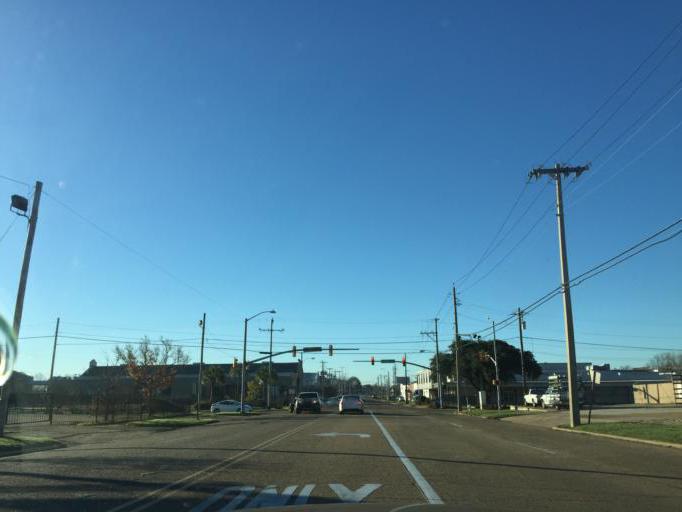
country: US
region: Mississippi
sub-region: Hinds County
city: Jackson
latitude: 32.2910
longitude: -90.1820
